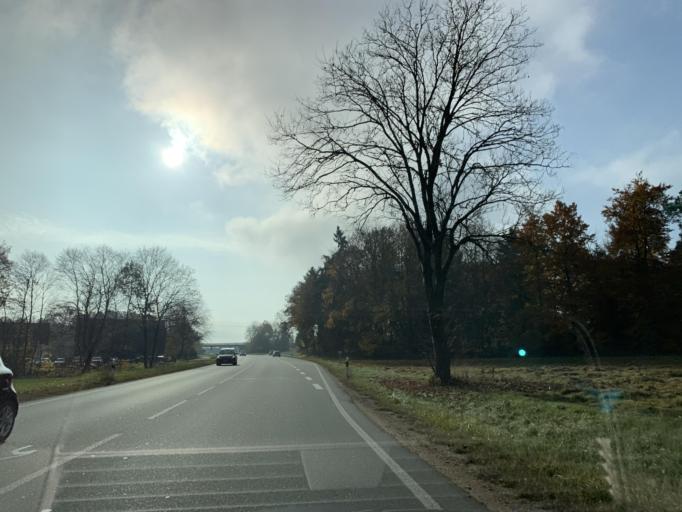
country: DE
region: Bavaria
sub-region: Upper Palatinate
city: Bruck in der Oberpfalz
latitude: 49.2603
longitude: 12.2968
